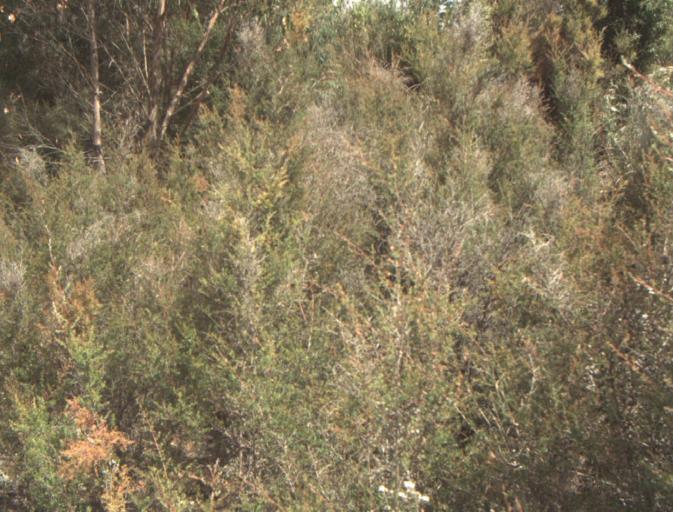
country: AU
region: Tasmania
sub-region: Launceston
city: Mayfield
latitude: -41.2035
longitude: 147.1624
